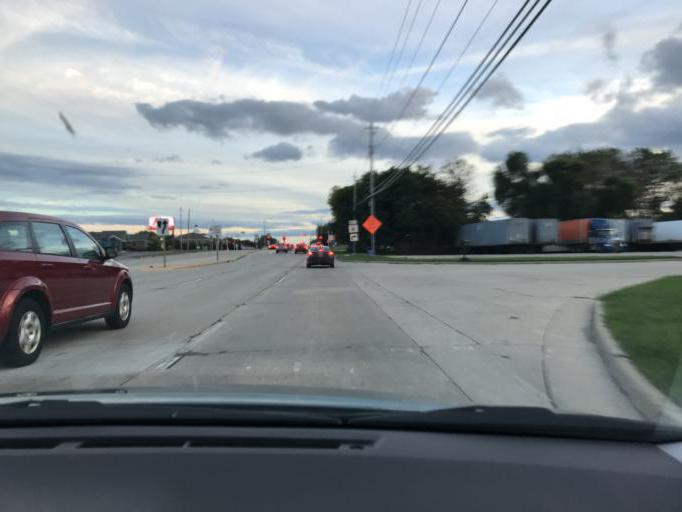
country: US
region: Wisconsin
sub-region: Kenosha County
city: Pleasant Prairie
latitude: 42.5837
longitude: -87.8837
